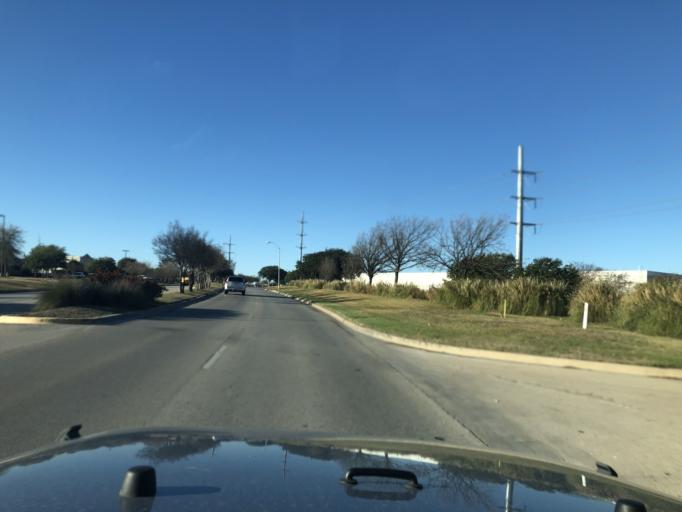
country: US
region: Texas
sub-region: Williamson County
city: Round Rock
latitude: 30.5353
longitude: -97.6829
